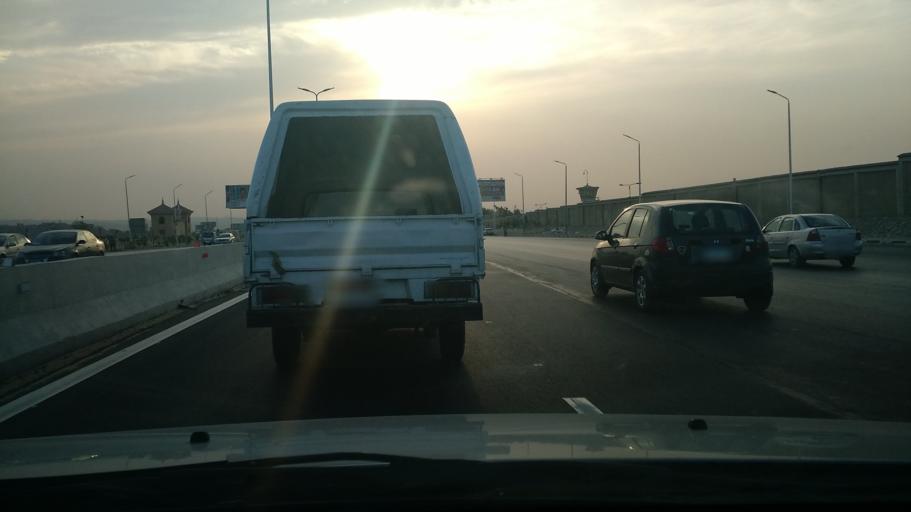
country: EG
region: Muhafazat al Qahirah
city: Cairo
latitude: 30.0234
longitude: 31.3667
